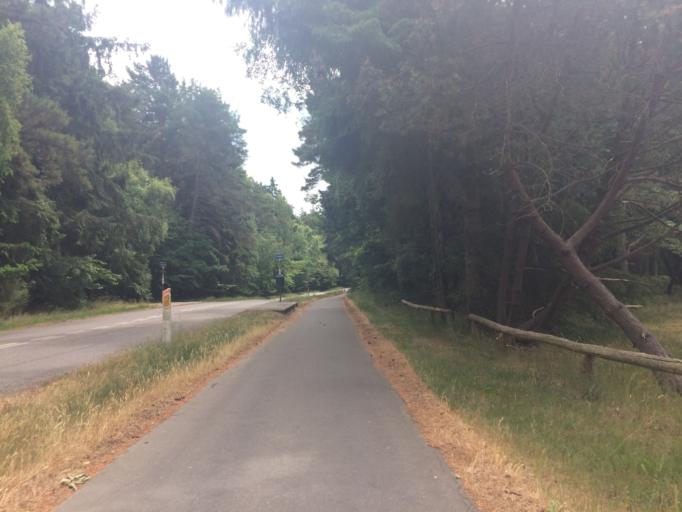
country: DK
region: Capital Region
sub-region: Bornholm Kommune
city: Ronne
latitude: 55.1673
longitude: 14.7138
